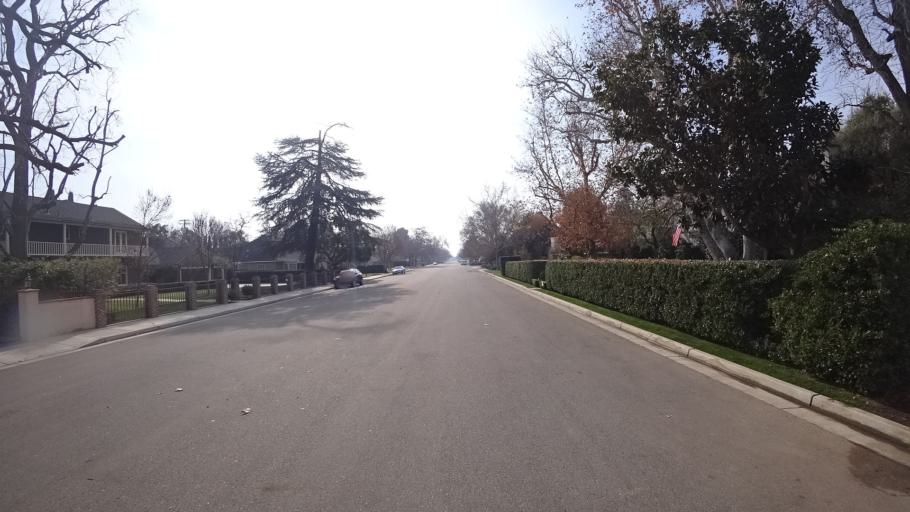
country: US
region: California
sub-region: Kern County
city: Bakersfield
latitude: 35.3802
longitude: -119.0317
